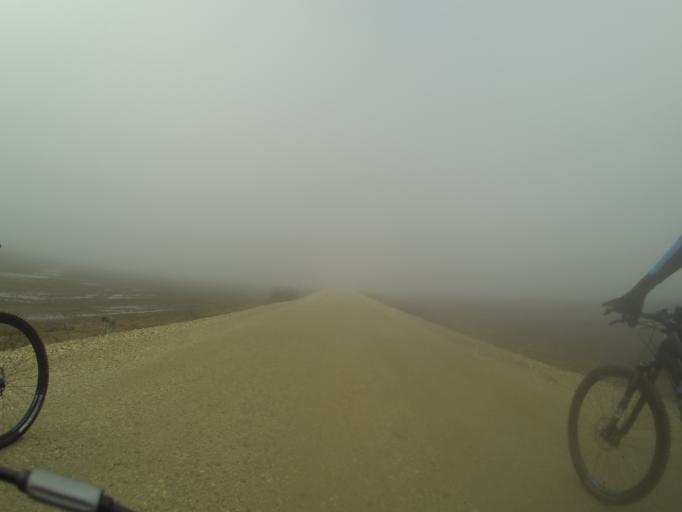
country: RO
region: Mehedinti
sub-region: Comuna Baclesu
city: Baclesu
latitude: 44.4425
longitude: 23.1304
